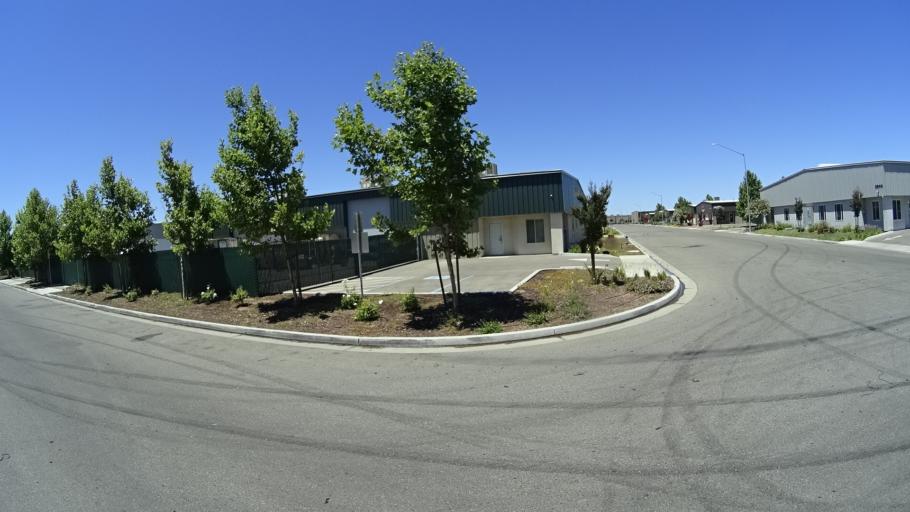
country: US
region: California
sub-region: Fresno County
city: West Park
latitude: 36.7985
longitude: -119.8584
